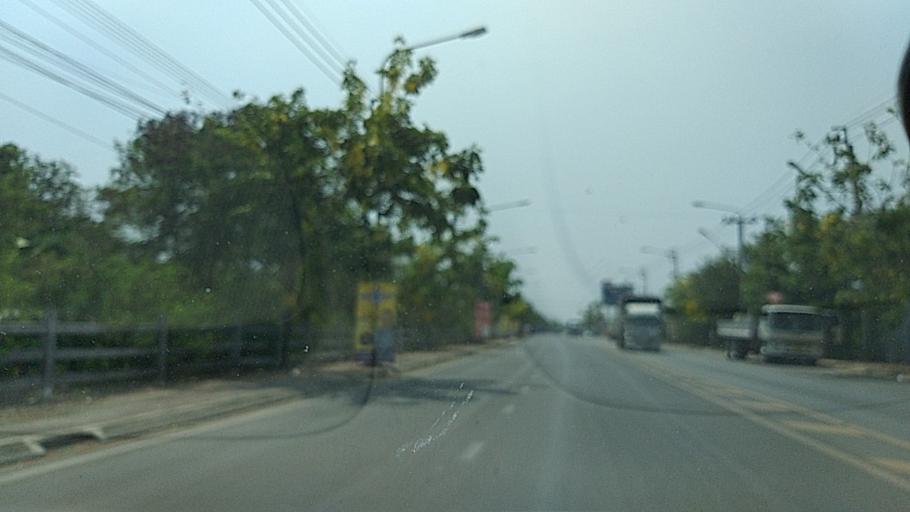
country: TH
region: Nonthaburi
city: Sai Noi
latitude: 13.9099
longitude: 100.3327
